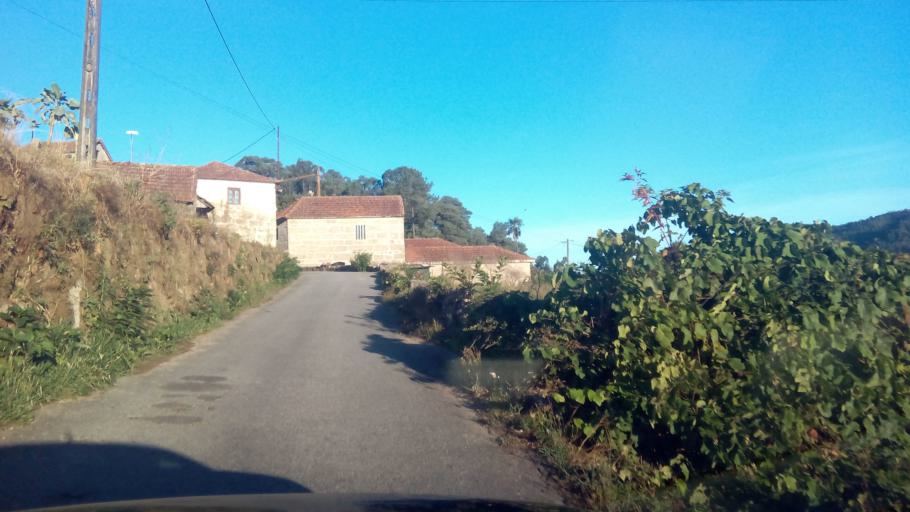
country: PT
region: Porto
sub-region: Paredes
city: Baltar
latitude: 41.1799
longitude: -8.3832
